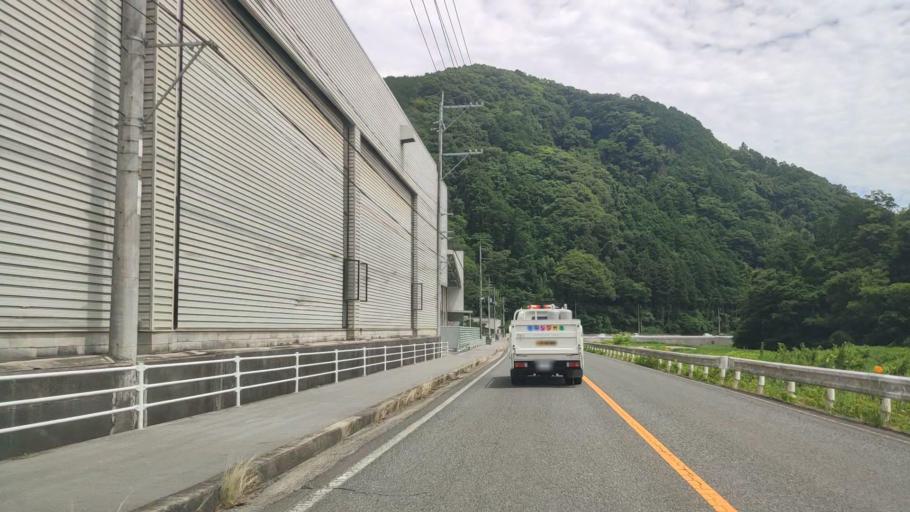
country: JP
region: Okayama
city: Niimi
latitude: 35.0723
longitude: 133.6803
